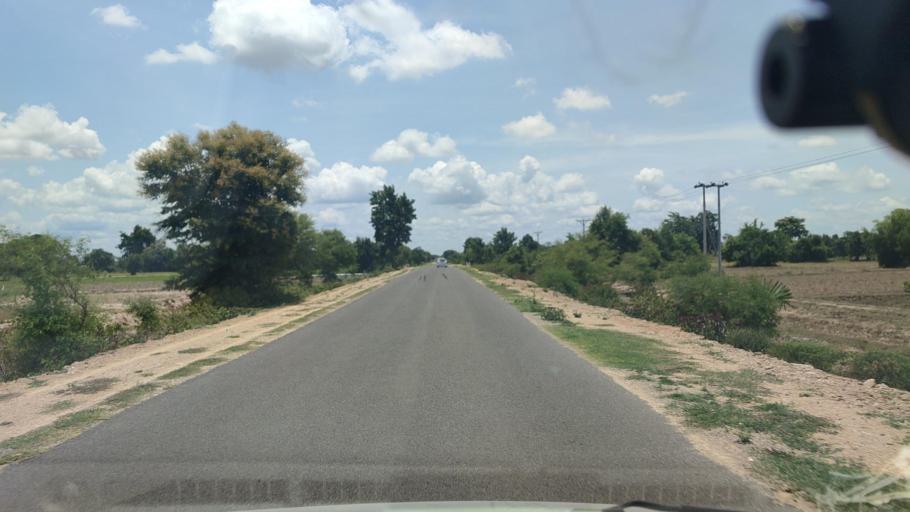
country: MM
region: Magway
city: Taungdwingyi
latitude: 20.1719
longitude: 95.4829
